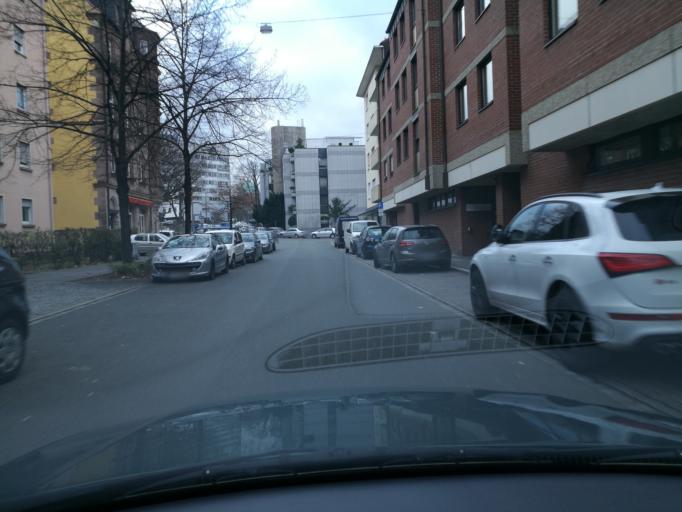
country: DE
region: Bavaria
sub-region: Regierungsbezirk Mittelfranken
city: Nuernberg
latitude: 49.4526
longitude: 11.0638
